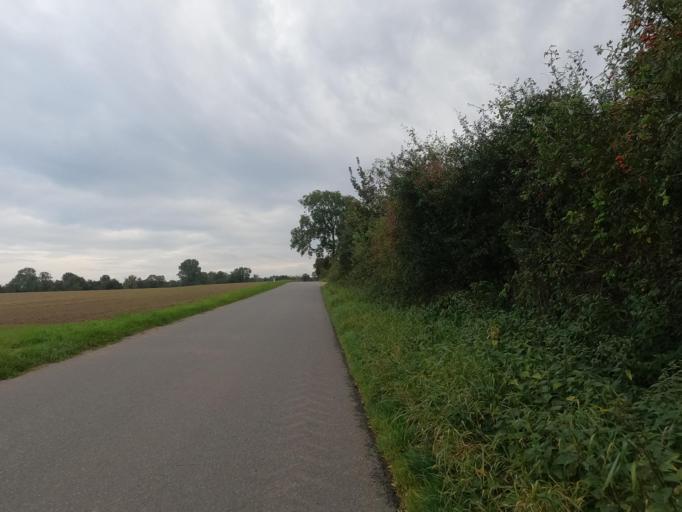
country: DE
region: Schleswig-Holstein
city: Neukirchen
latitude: 54.3075
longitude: 11.0439
